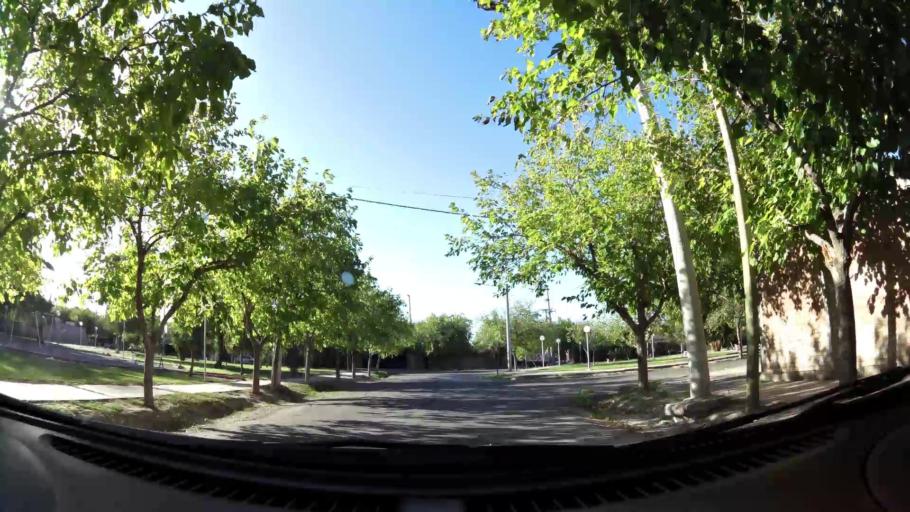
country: AR
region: San Juan
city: Villa Krause
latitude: -31.5607
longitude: -68.5163
